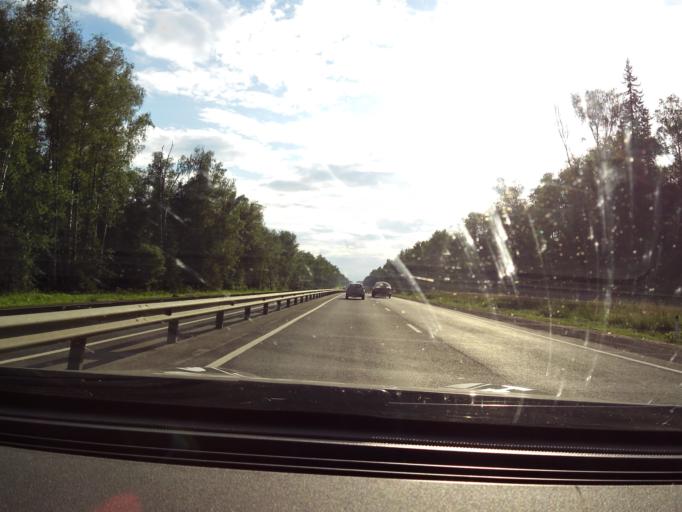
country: RU
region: Vladimir
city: Kameshkovo
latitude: 56.1995
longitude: 41.0573
